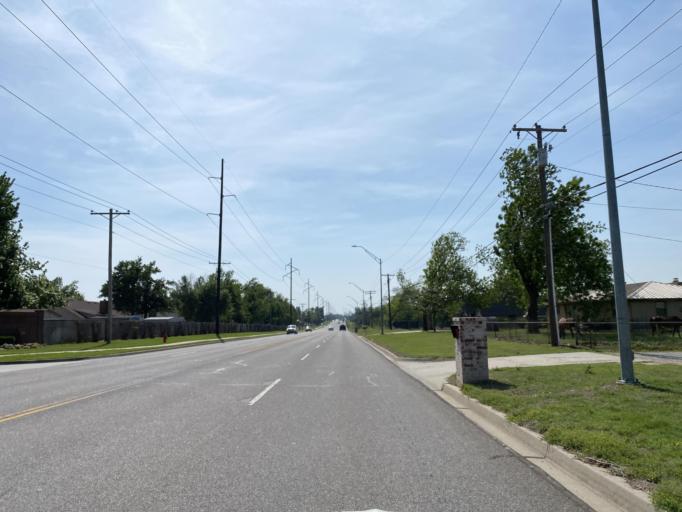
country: US
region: Oklahoma
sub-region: Oklahoma County
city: Nicoma Park
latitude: 35.4499
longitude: -97.3421
